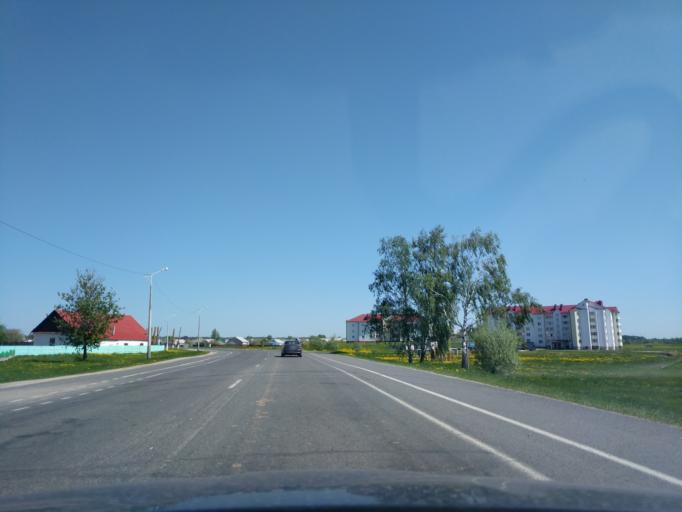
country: BY
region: Minsk
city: Myadzyel
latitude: 54.8738
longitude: 26.9399
